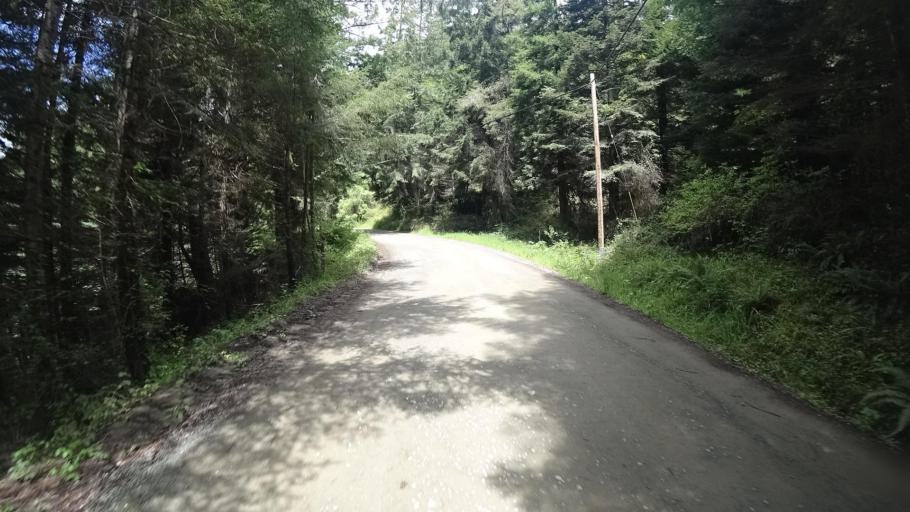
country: US
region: California
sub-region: Humboldt County
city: Blue Lake
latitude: 40.8074
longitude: -123.8840
